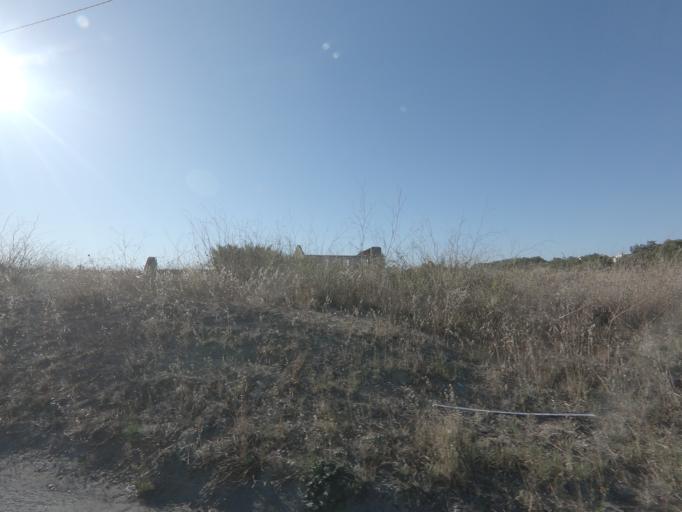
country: PT
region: Setubal
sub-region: Palmela
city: Quinta do Anjo
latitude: 38.5614
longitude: -8.9527
